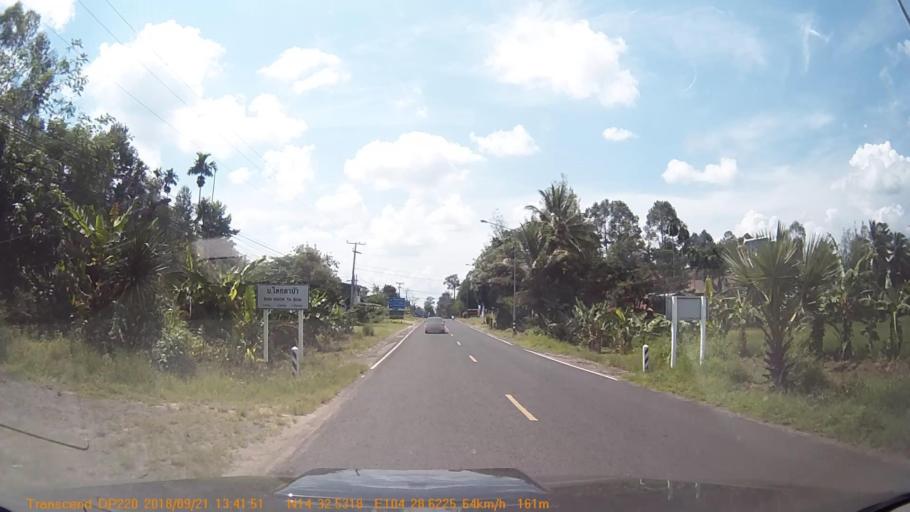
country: TH
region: Sisaket
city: Khun Han
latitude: 14.5424
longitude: 104.4766
